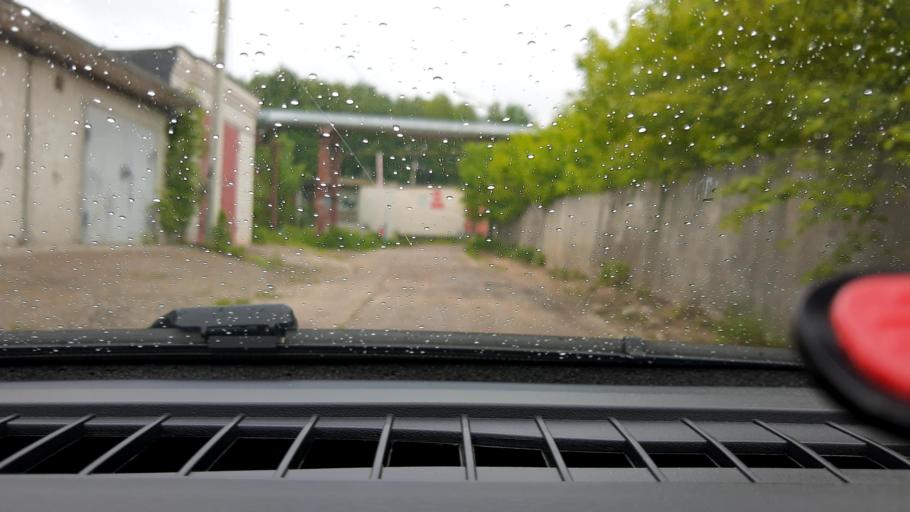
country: RU
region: Nizjnij Novgorod
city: Bor
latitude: 56.3127
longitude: 44.0602
